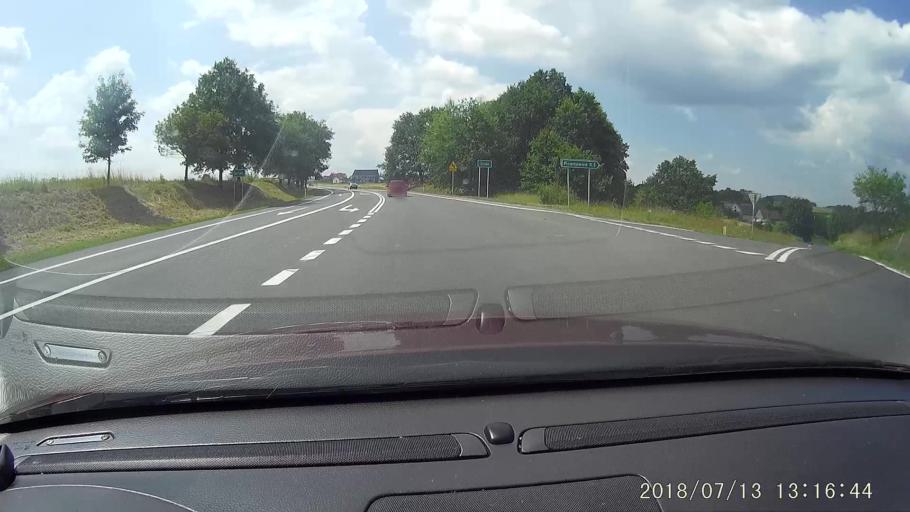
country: PL
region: Lower Silesian Voivodeship
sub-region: Powiat lubanski
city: Luban
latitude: 51.1335
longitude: 15.2682
